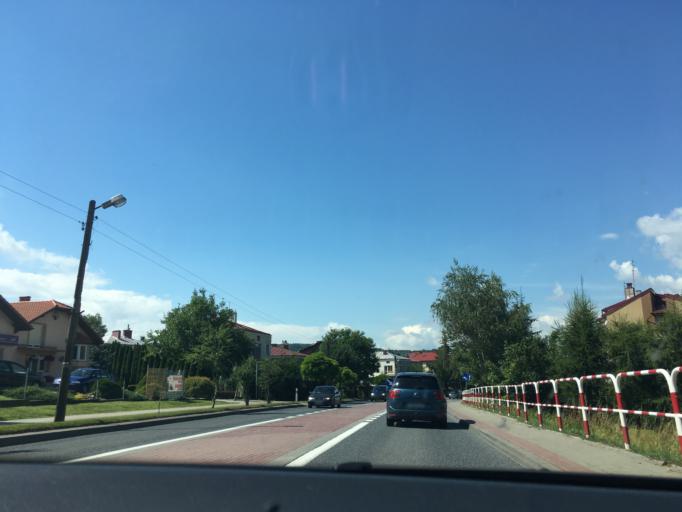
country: PL
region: Subcarpathian Voivodeship
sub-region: Powiat krosnienski
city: Dukla
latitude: 49.5501
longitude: 21.6834
